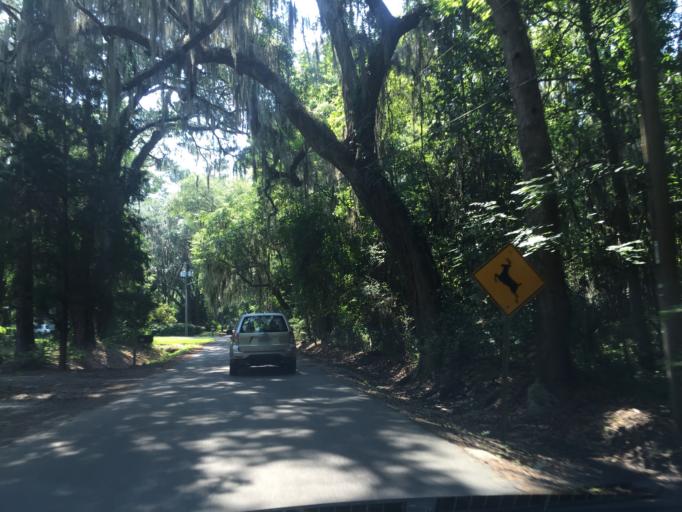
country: US
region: Georgia
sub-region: Chatham County
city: Montgomery
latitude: 31.9656
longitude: -81.1333
